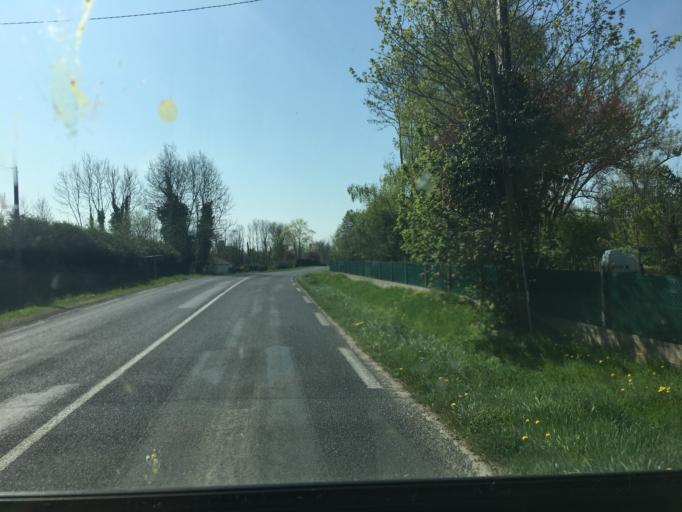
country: FR
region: Lorraine
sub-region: Departement de Meurthe-et-Moselle
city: Norroy-les-Pont-a-Mousson
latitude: 48.9274
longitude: 6.0382
